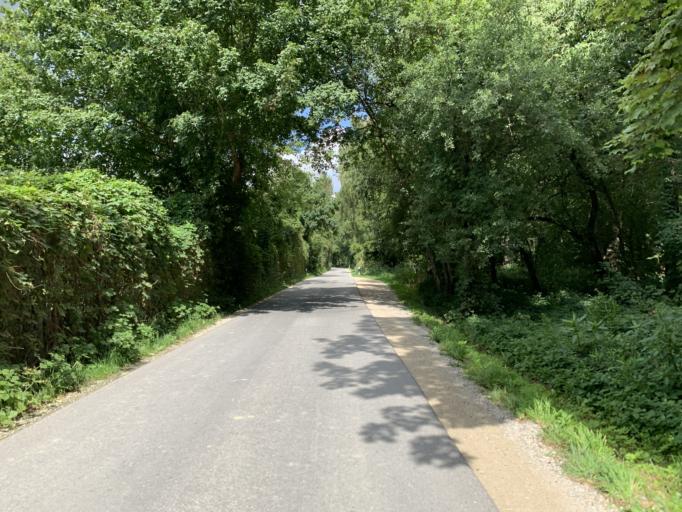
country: DE
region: Bavaria
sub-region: Upper Bavaria
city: Zolling
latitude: 48.4421
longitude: 11.7900
